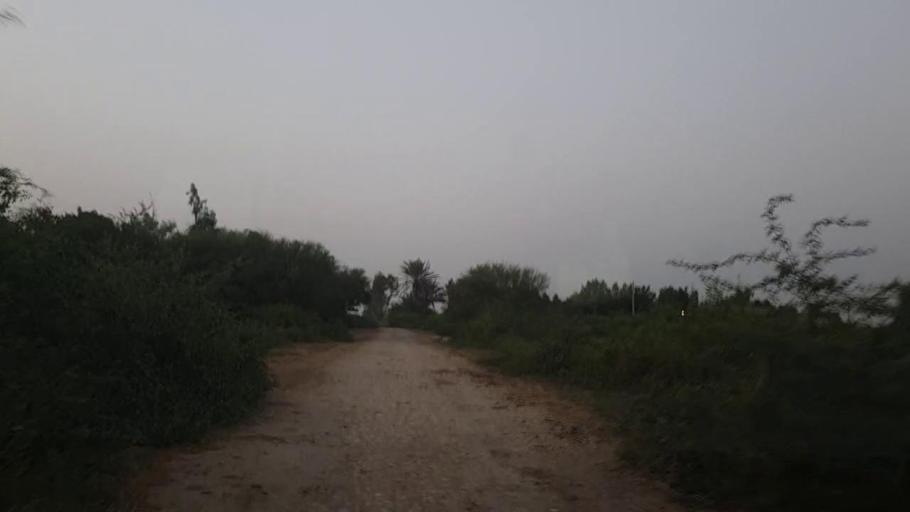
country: PK
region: Sindh
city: Mirpur Sakro
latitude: 24.5878
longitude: 67.7835
